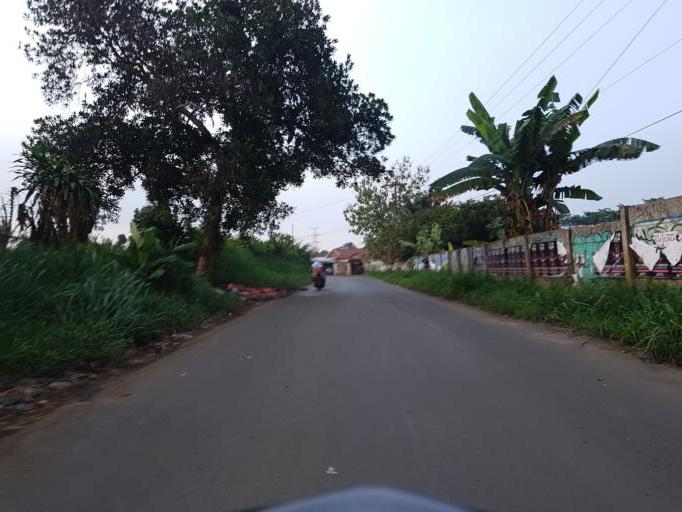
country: ID
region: West Java
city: Parung
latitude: -6.4714
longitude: 106.7182
